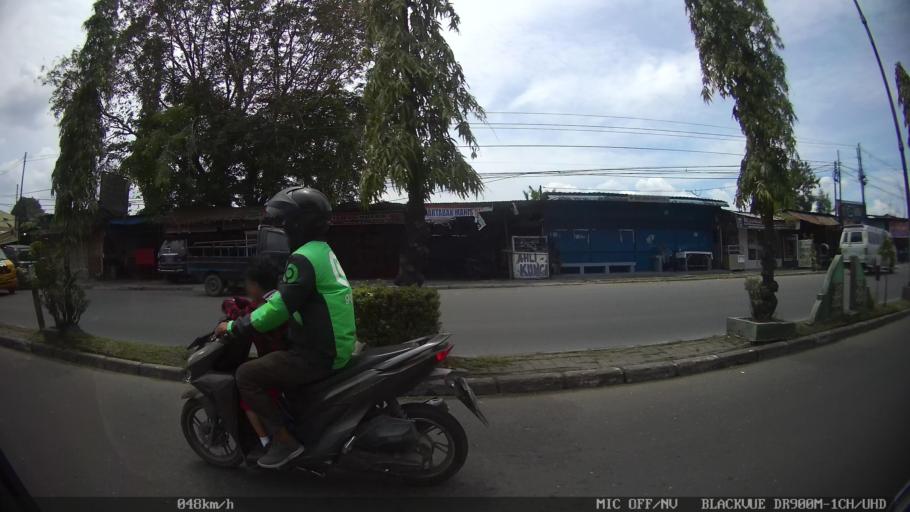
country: ID
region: North Sumatra
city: Medan
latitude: 3.5457
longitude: 98.6587
